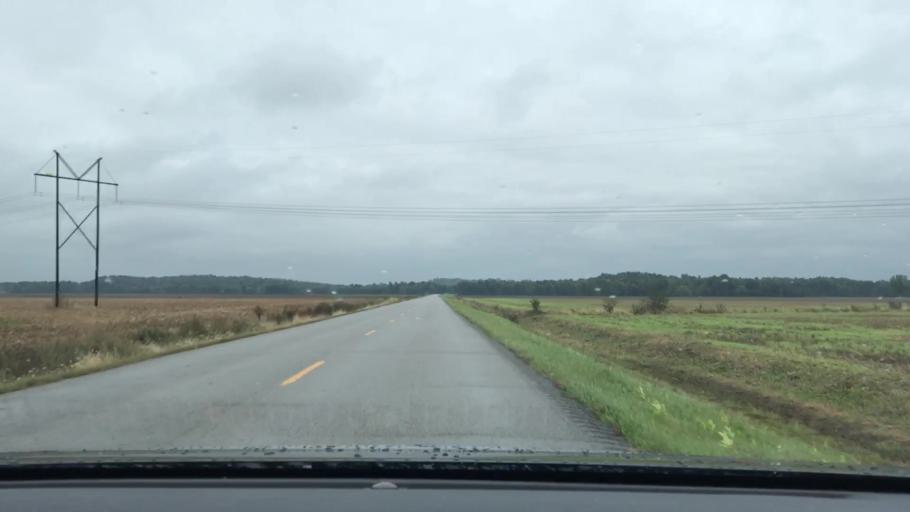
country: US
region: Kentucky
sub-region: McLean County
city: Calhoun
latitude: 37.5043
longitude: -87.2498
